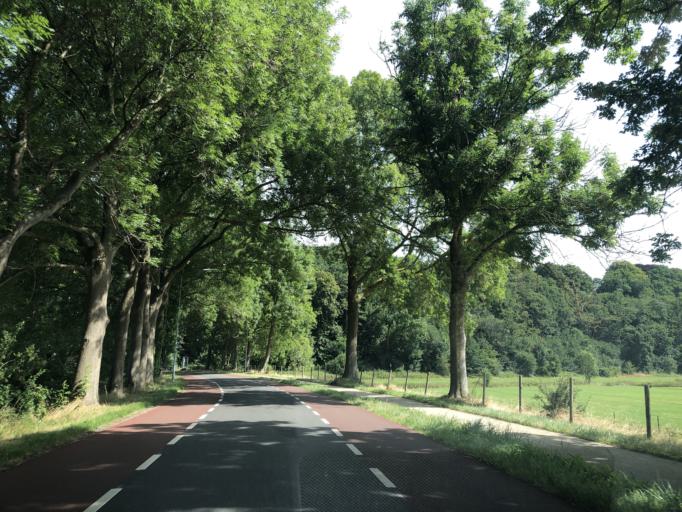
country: NL
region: Gelderland
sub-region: Gemeente Wageningen
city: Wageningen
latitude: 51.9632
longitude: 5.6881
